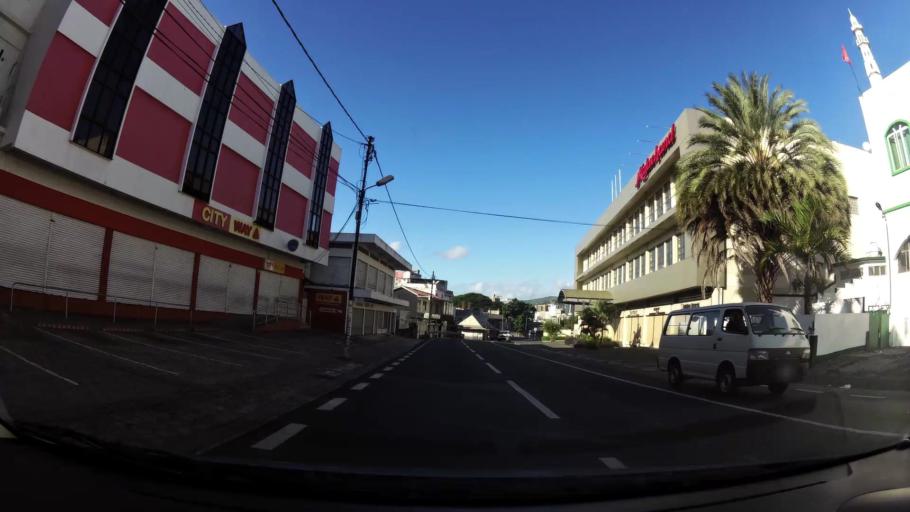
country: MU
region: Port Louis
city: Port Louis
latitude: -20.1657
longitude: 57.4907
